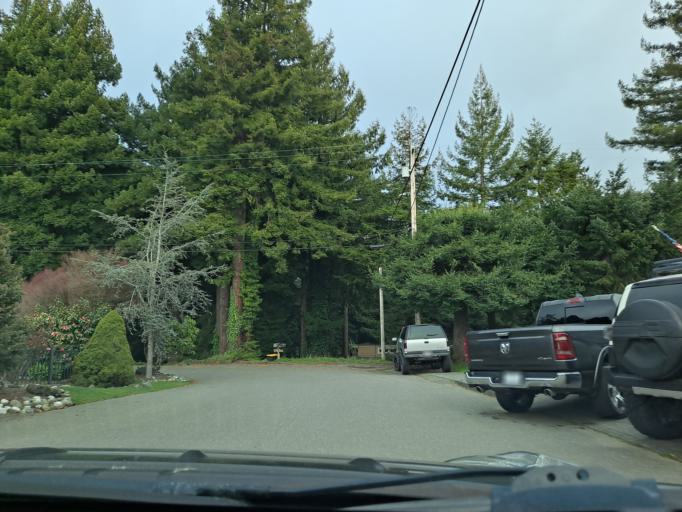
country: US
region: California
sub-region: Humboldt County
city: Fortuna
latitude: 40.6038
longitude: -124.1547
